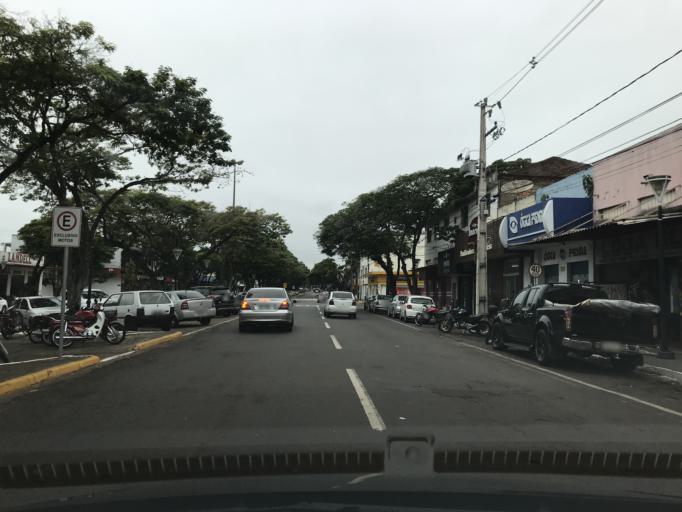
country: PY
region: Canindeyu
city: Salto del Guaira
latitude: -24.0811
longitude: -54.2535
